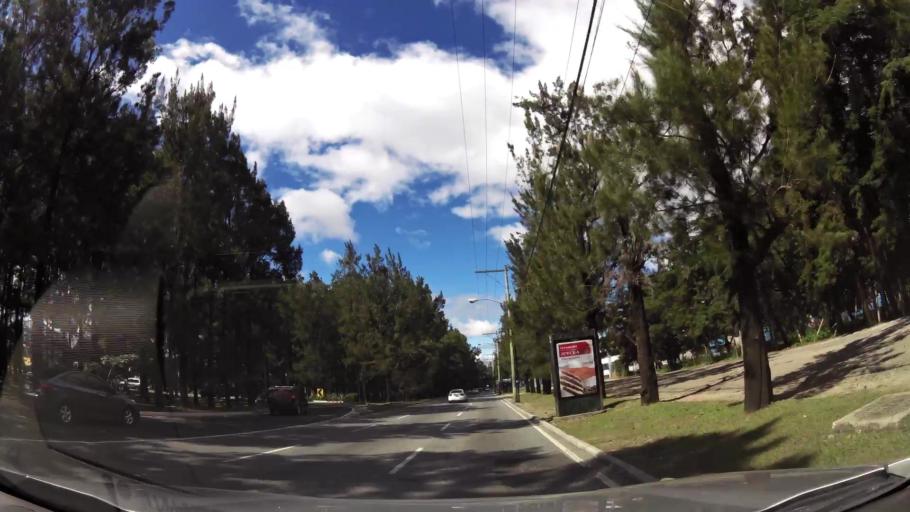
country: GT
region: Guatemala
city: Santa Catarina Pinula
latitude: 14.6016
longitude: -90.4994
